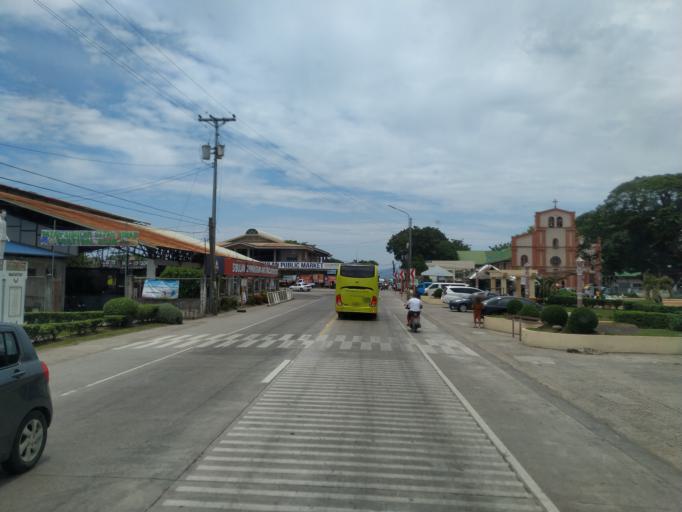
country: PH
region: Central Visayas
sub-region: Province of Negros Oriental
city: Sibulan
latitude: 9.3588
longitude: 123.2851
